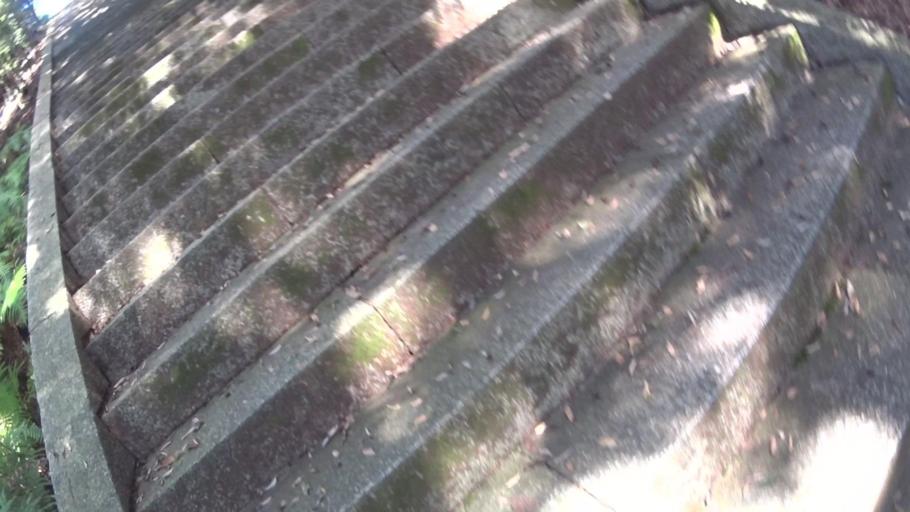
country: RU
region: Rostov
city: Remontnoye
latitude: 46.5004
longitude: 43.7662
